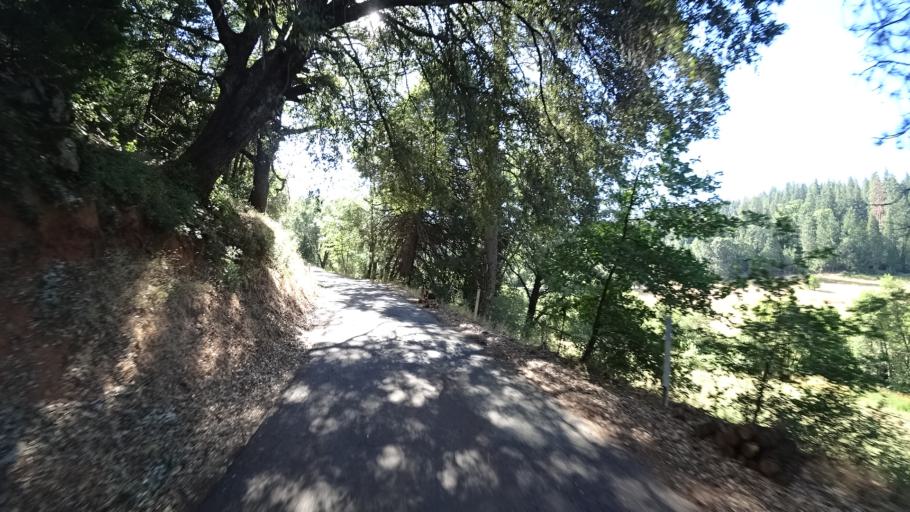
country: US
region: California
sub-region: Amador County
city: Pioneer
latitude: 38.3886
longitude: -120.4485
